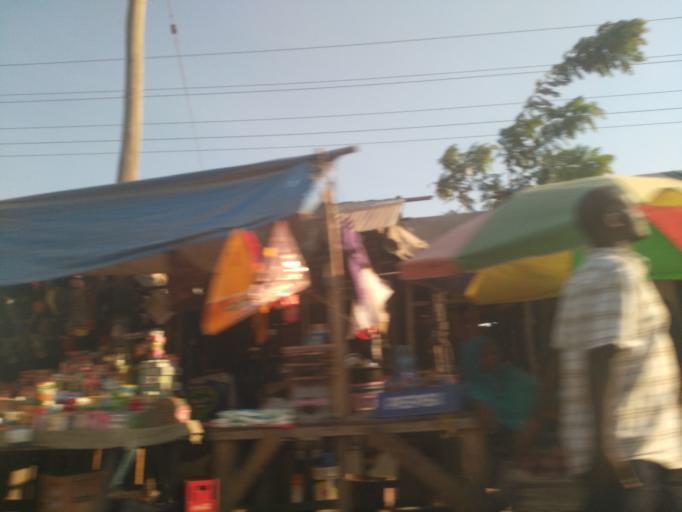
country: TZ
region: Pwani
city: Vikindu
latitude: -6.9196
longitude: 39.2682
